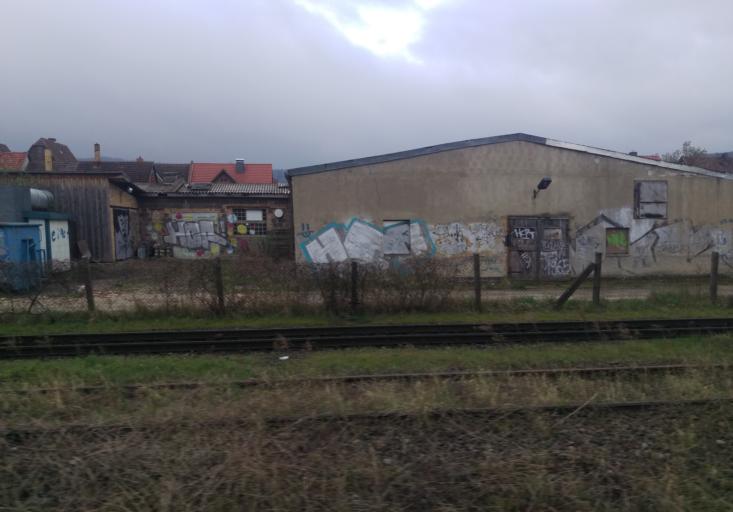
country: DE
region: Saxony-Anhalt
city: Wernigerode
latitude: 51.8384
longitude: 10.7759
